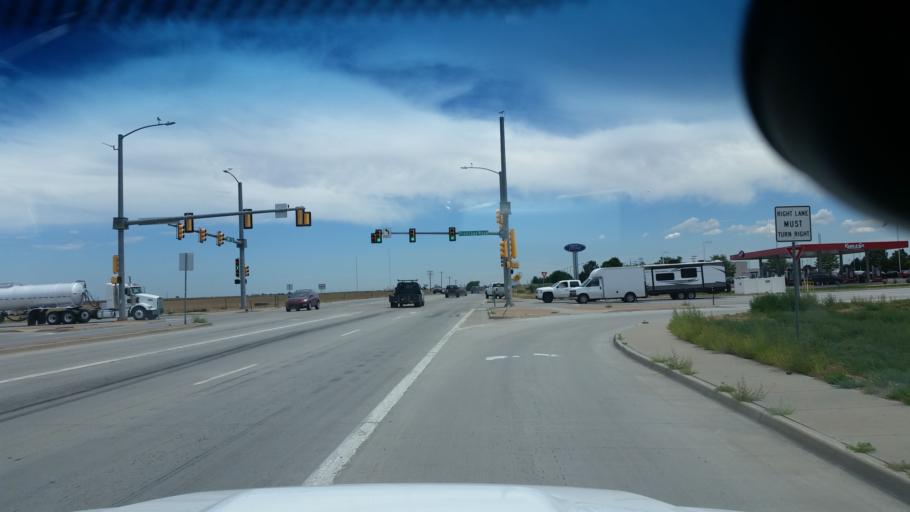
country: US
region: Colorado
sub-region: Weld County
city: Dacono
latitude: 40.0876
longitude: -104.9759
